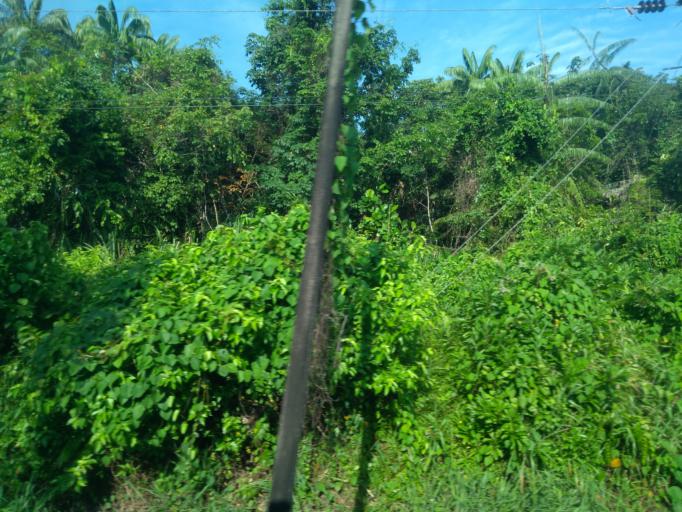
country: MY
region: Sarawak
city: Kuching
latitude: 1.6479
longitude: 110.4471
